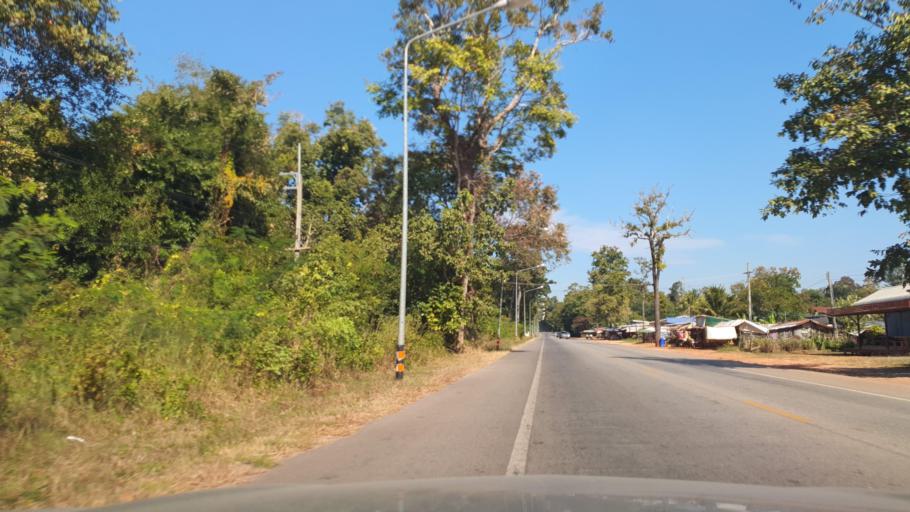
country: TH
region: Sakon Nakhon
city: Phu Phan
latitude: 17.0974
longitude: 103.9896
